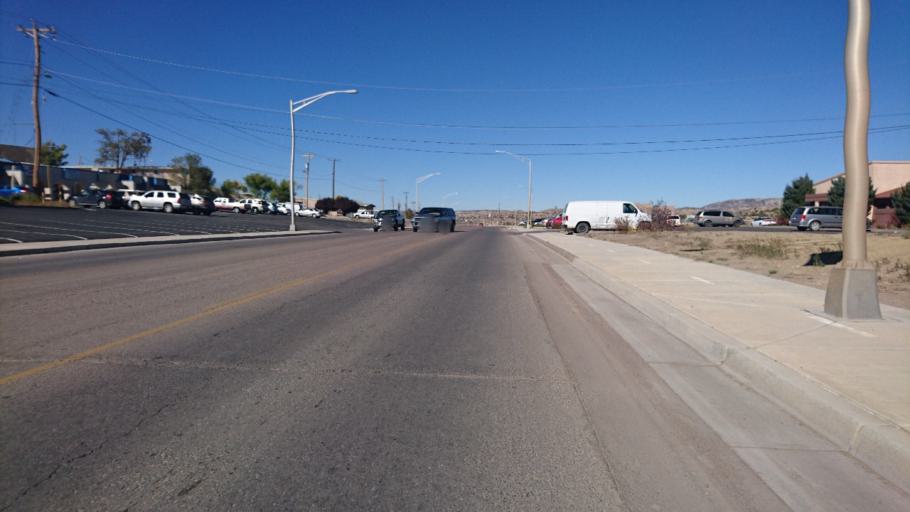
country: US
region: New Mexico
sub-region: McKinley County
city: Gallup
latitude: 35.5128
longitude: -108.7386
